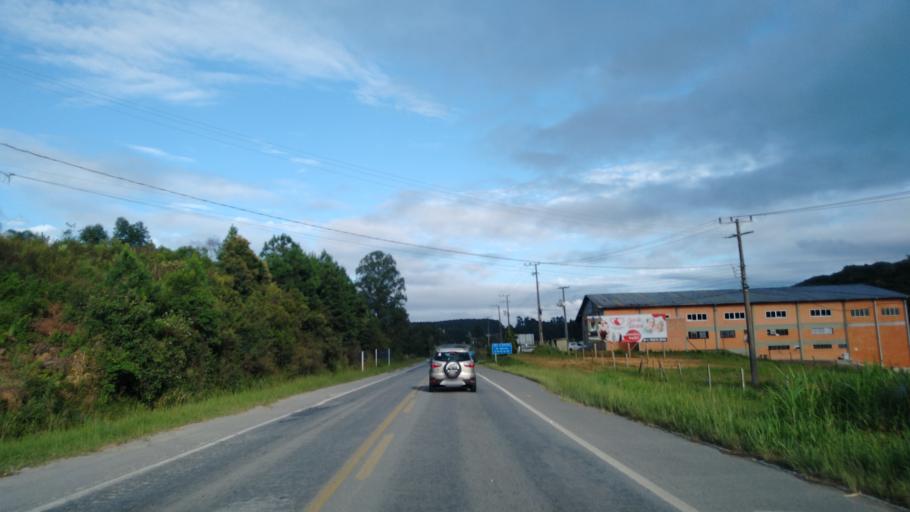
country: BR
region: Santa Catarina
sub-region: Rio Negrinho
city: Rio Negrinho
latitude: -26.2433
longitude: -49.4687
